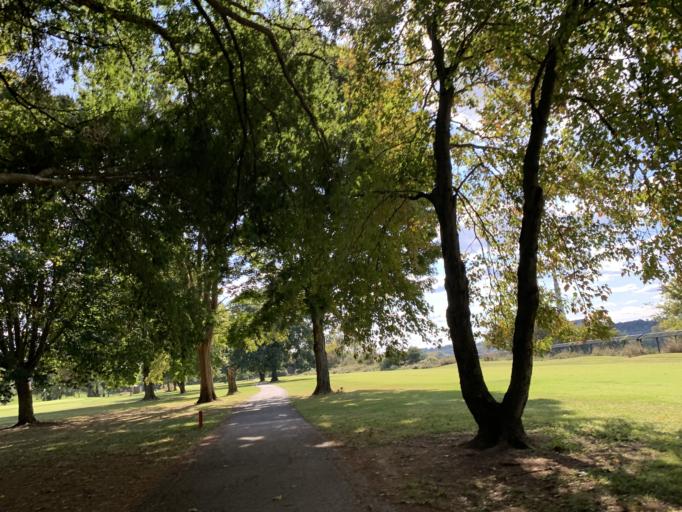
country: US
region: Indiana
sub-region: Floyd County
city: New Albany
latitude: 38.2697
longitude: -85.8268
